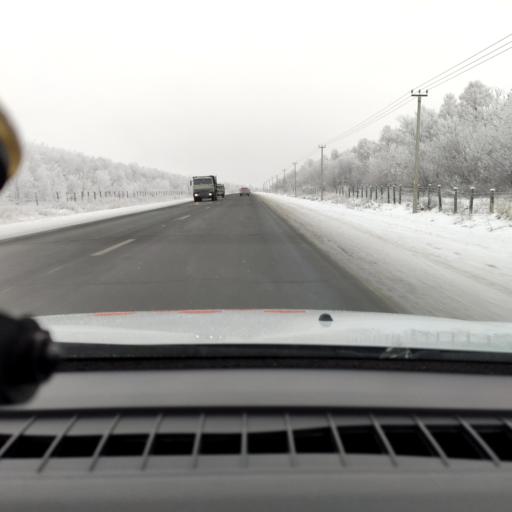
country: RU
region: Samara
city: Chapayevsk
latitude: 52.9966
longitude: 49.7963
